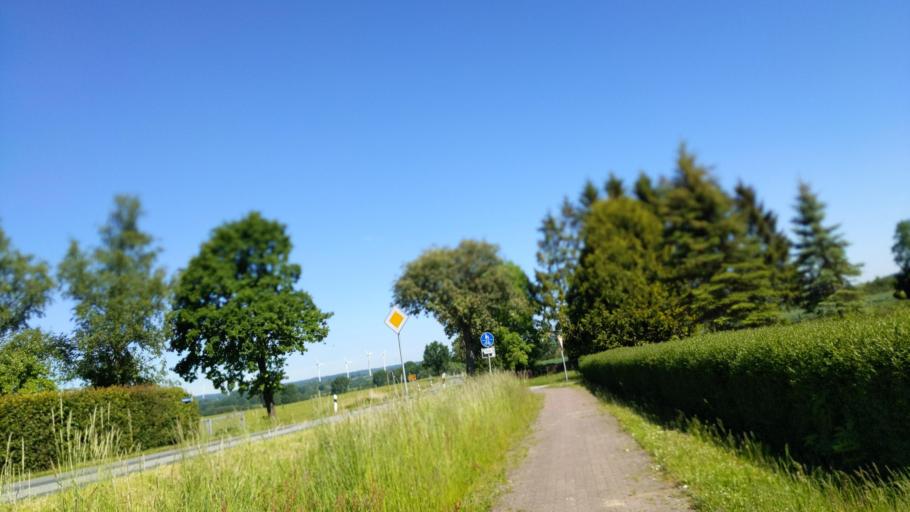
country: DE
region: Schleswig-Holstein
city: Altenkrempe
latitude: 54.1377
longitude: 10.8484
